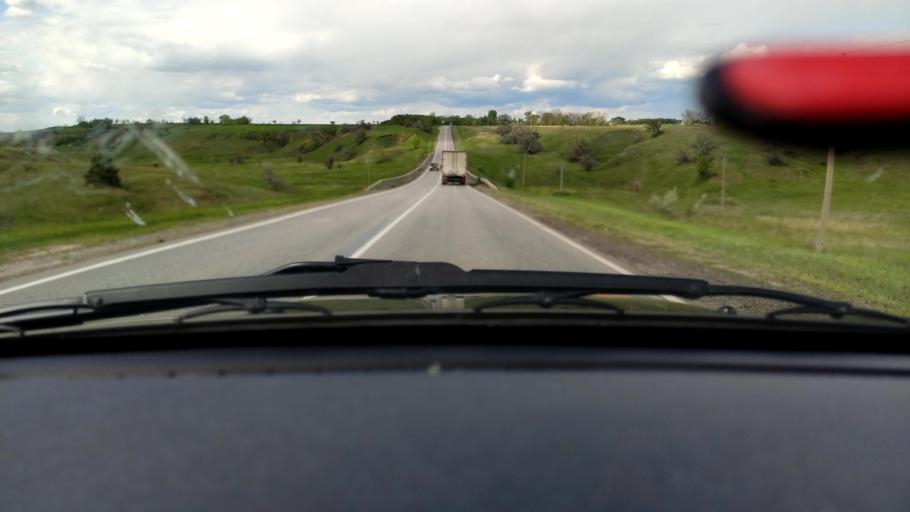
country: RU
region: Voronezj
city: Uryv-Pokrovka
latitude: 51.0702
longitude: 38.9956
